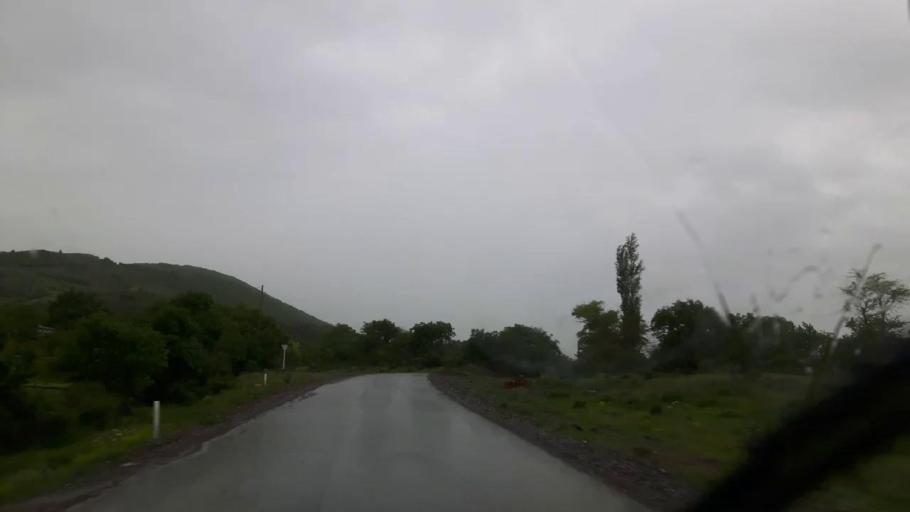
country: GE
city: Agara
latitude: 41.9813
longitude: 43.9421
